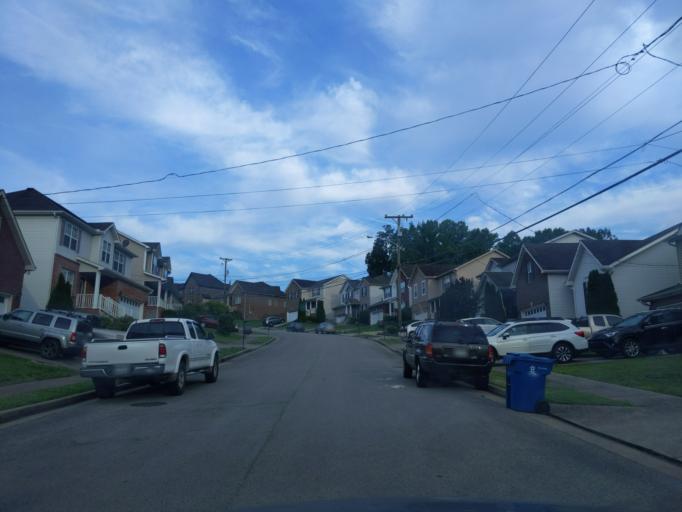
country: US
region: Tennessee
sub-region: Wilson County
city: Green Hill
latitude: 36.1812
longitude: -86.5956
